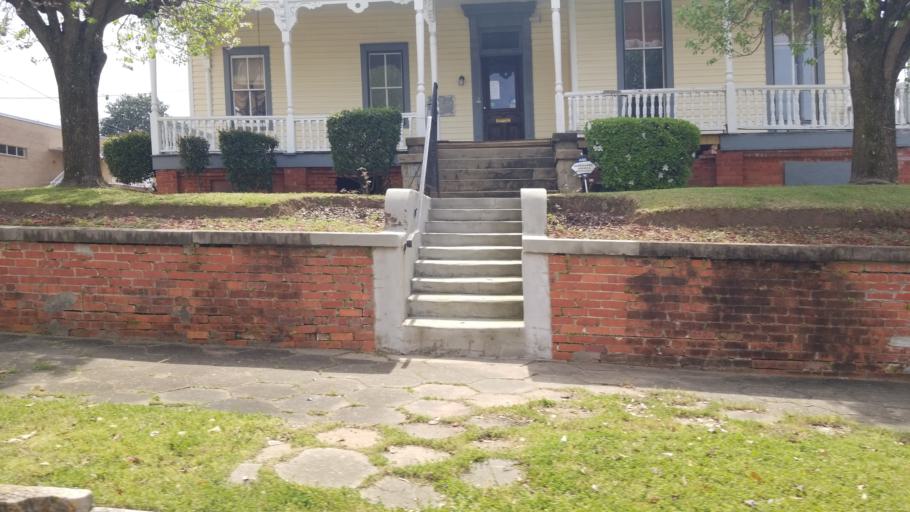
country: US
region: Alabama
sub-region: Montgomery County
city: Montgomery
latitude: 32.3711
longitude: -86.3098
